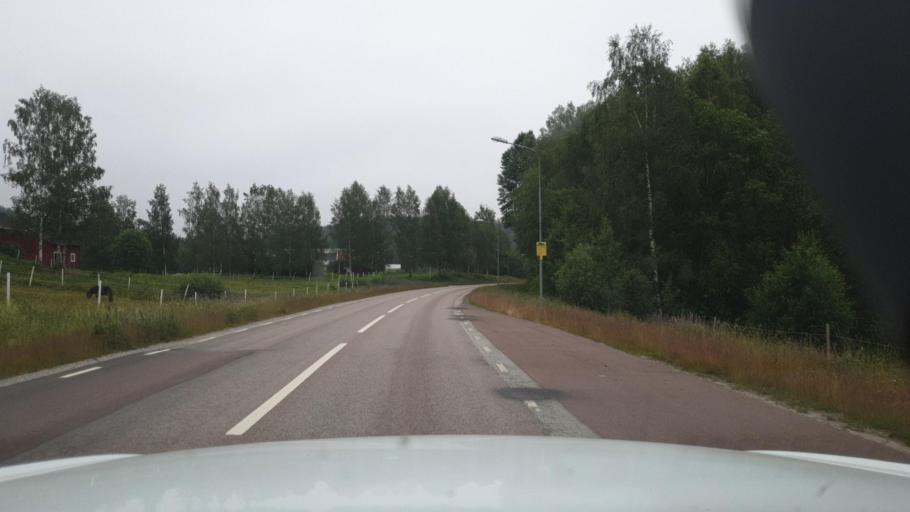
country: SE
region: Vaermland
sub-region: Arvika Kommun
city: Arvika
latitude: 59.6464
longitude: 12.7729
